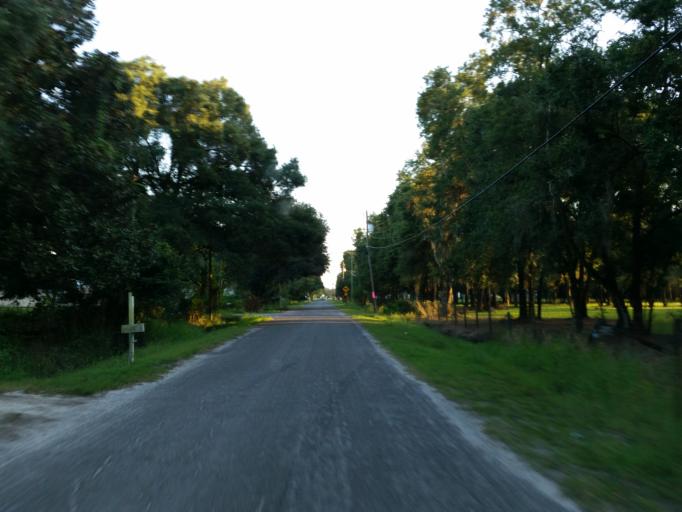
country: US
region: Florida
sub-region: Hillsborough County
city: Dover
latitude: 28.0459
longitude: -82.2438
